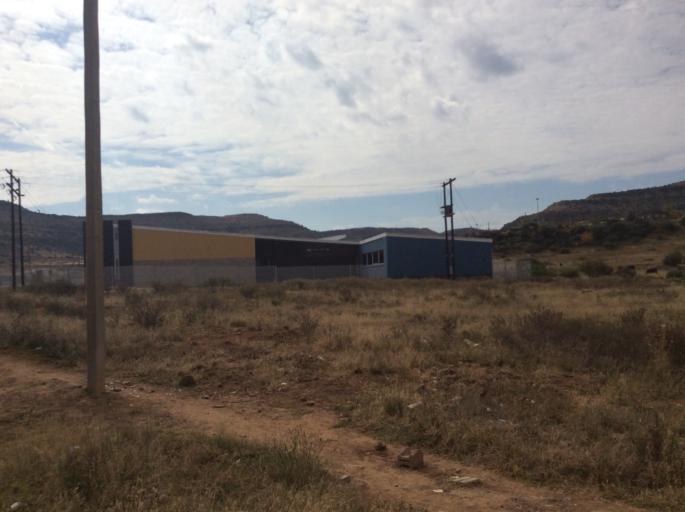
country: LS
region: Mafeteng
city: Mafeteng
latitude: -29.7219
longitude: 27.0253
